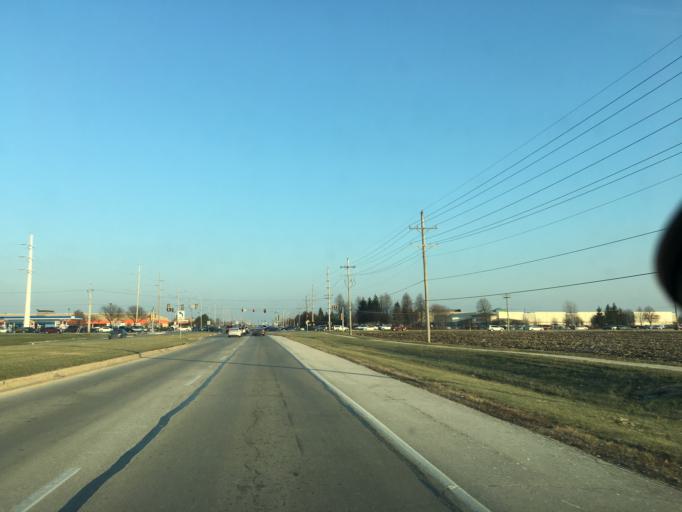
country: US
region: Illinois
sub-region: DuPage County
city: Naperville
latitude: 41.7470
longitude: -88.2084
